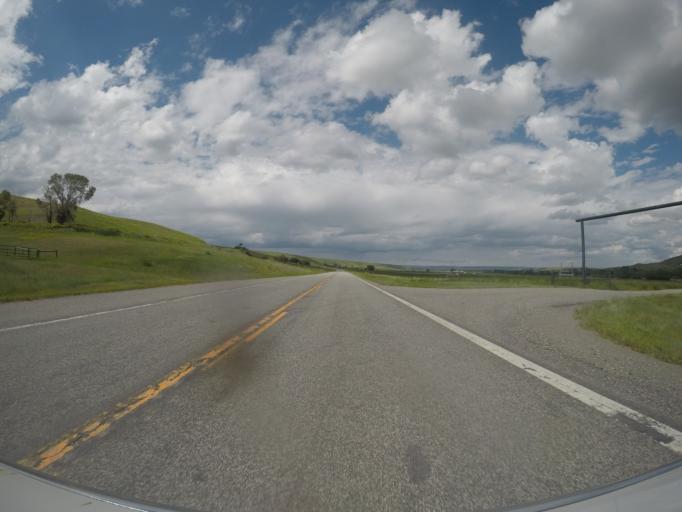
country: US
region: Montana
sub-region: Sweet Grass County
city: Big Timber
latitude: 45.7593
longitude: -109.9905
